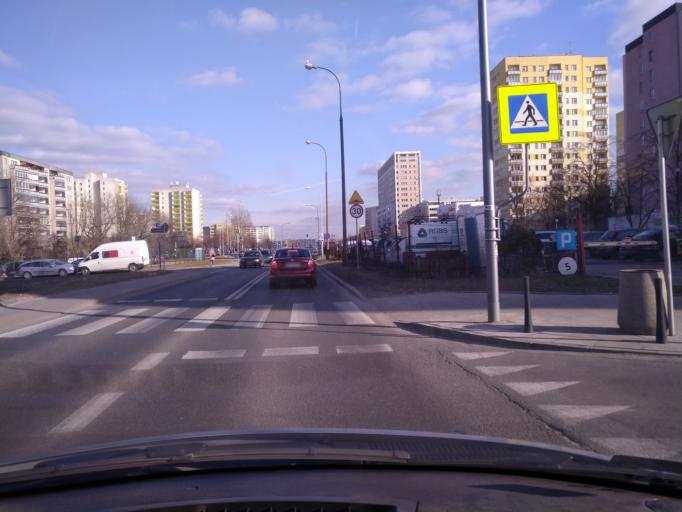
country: PL
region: Masovian Voivodeship
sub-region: Warszawa
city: Praga Poludnie
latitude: 52.2255
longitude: 21.0890
